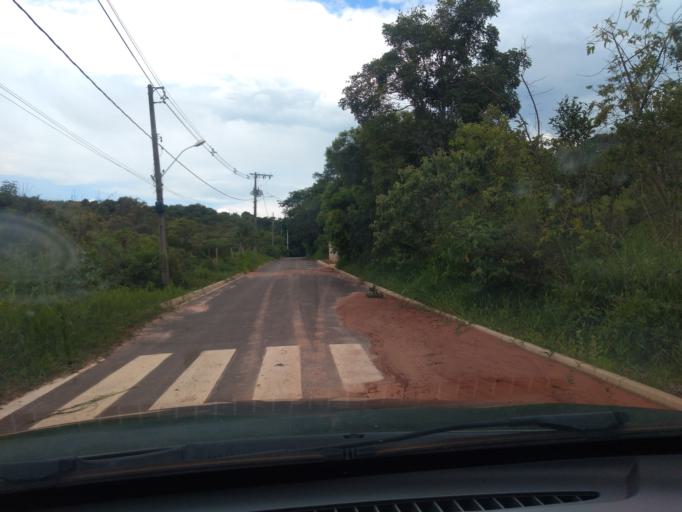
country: BR
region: Minas Gerais
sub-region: Tres Coracoes
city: Tres Coracoes
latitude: -21.6872
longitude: -45.2717
